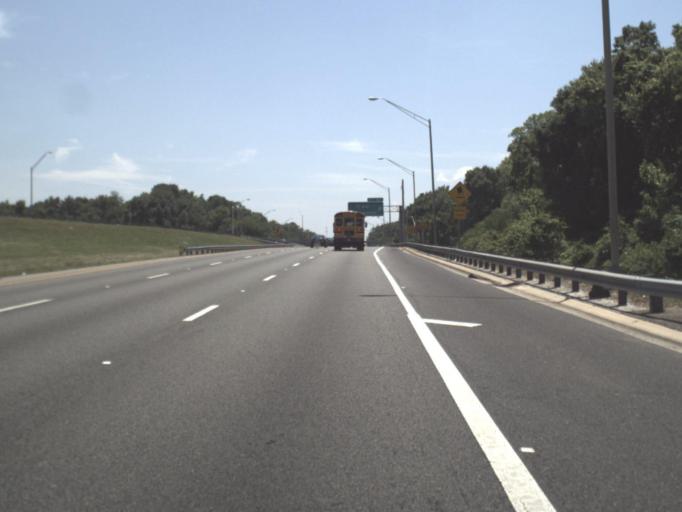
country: US
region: Florida
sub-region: Duval County
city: Jacksonville
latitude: 30.3174
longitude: -81.7706
